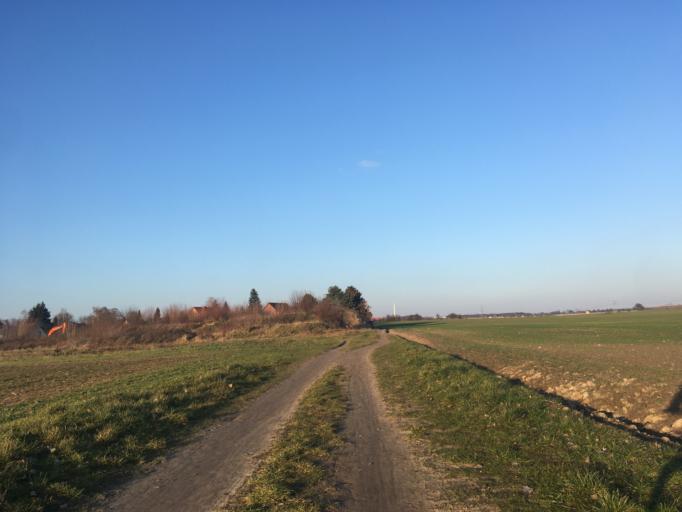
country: DE
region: Berlin
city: Karow
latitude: 52.6054
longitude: 13.4967
